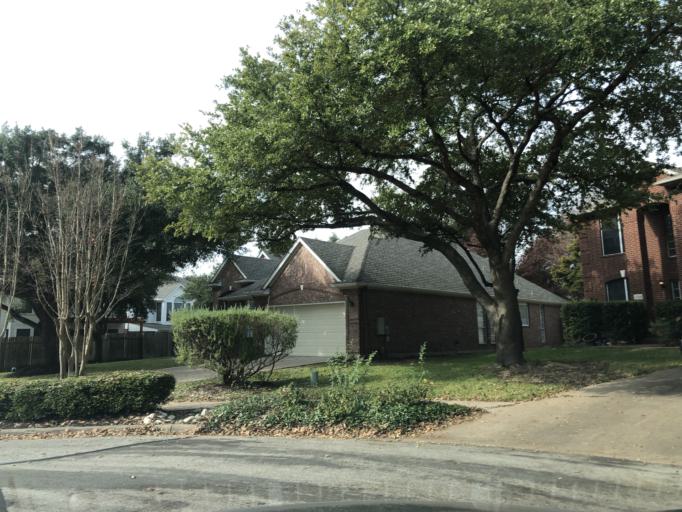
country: US
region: Texas
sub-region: Travis County
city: Wells Branch
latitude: 30.4219
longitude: -97.6804
